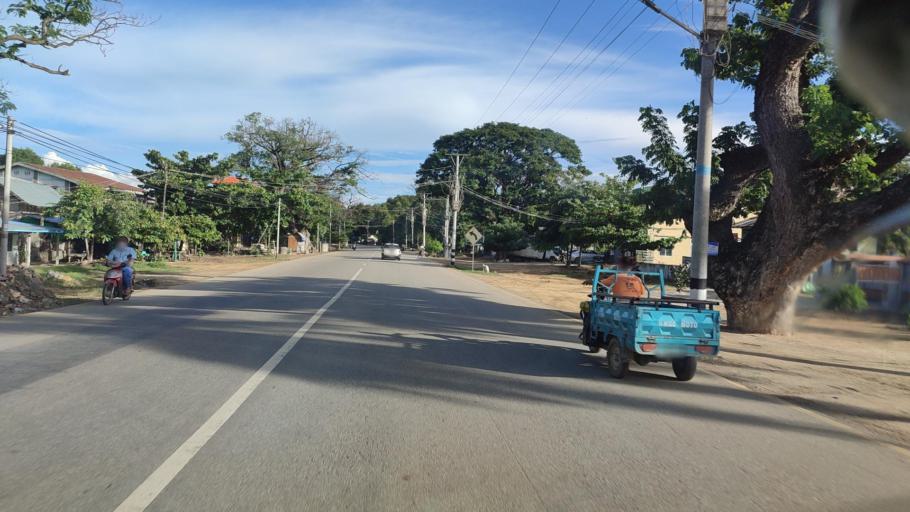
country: MM
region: Mandalay
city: Yamethin
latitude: 20.1376
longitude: 96.1973
